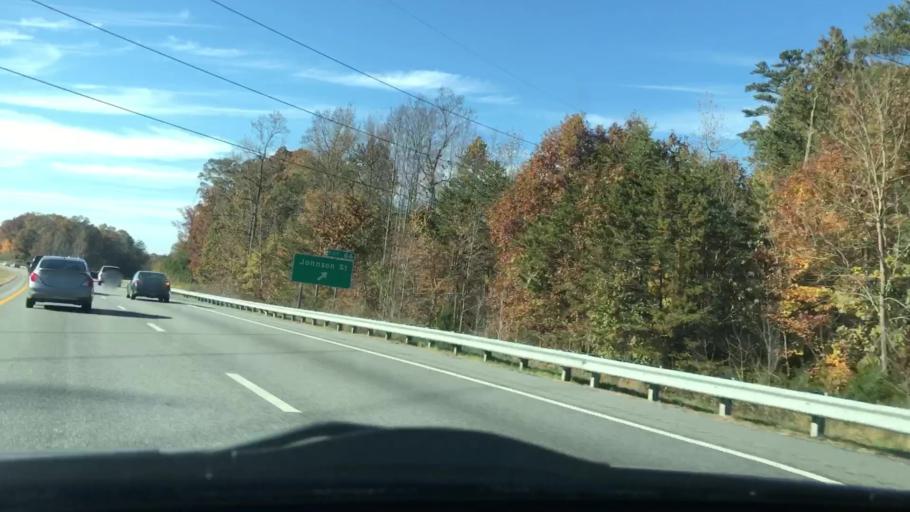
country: US
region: North Carolina
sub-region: Guilford County
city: High Point
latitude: 36.0084
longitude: -80.0044
